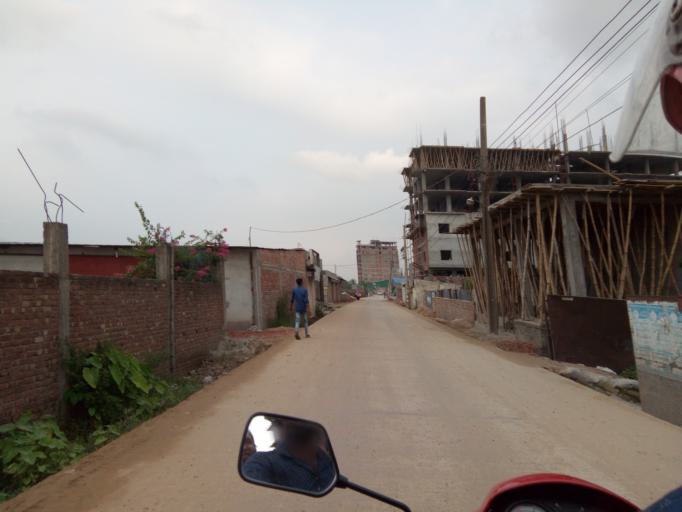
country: BD
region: Dhaka
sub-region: Dhaka
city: Dhaka
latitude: 23.7021
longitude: 90.4729
